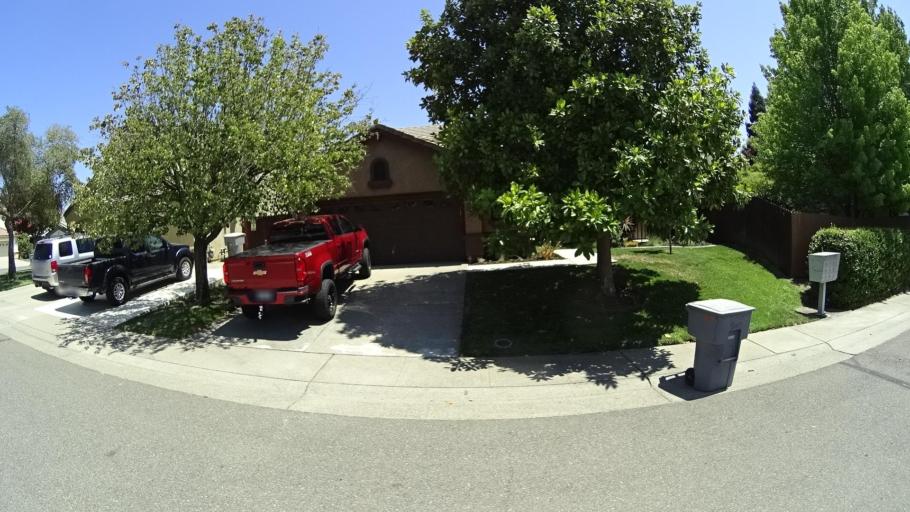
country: US
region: California
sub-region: Placer County
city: Rocklin
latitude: 38.8179
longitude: -121.2550
